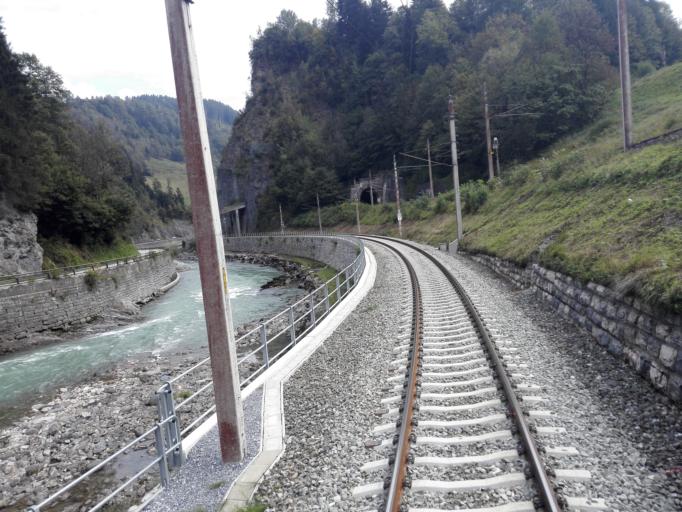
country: AT
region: Salzburg
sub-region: Politischer Bezirk Sankt Johann im Pongau
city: Goldegg
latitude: 47.3031
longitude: 13.1094
